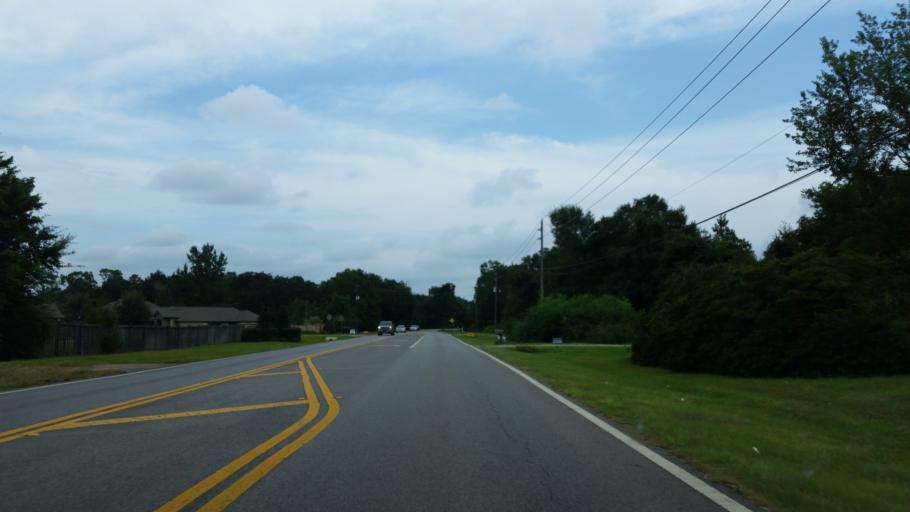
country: US
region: Florida
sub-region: Santa Rosa County
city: Pace
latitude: 30.6252
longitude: -87.1645
